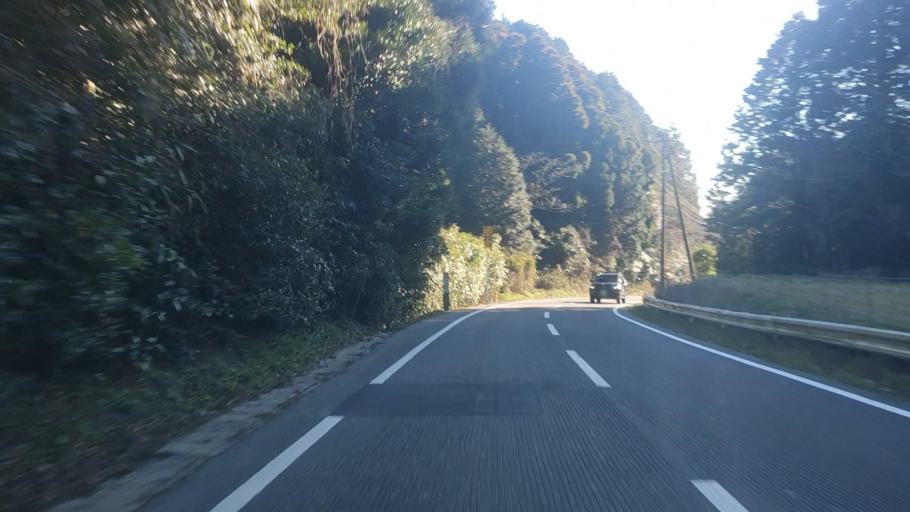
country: JP
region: Saga Prefecture
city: Kanzakimachi-kanzaki
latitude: 33.3975
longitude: 130.2717
